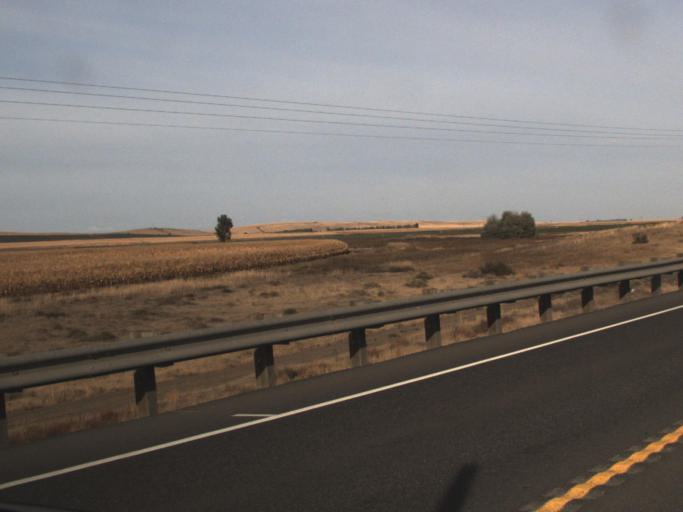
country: US
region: Oregon
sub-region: Morrow County
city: Irrigon
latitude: 45.9463
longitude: -119.4702
